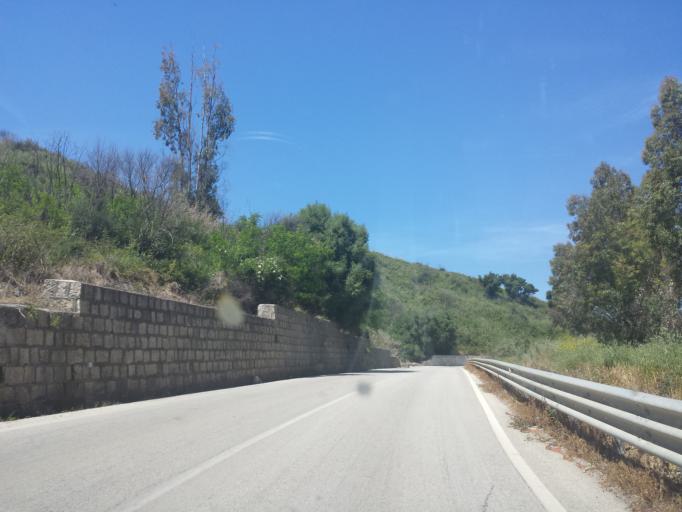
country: IT
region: Sicily
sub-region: Trapani
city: Calatafimi
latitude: 37.9583
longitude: 12.8744
